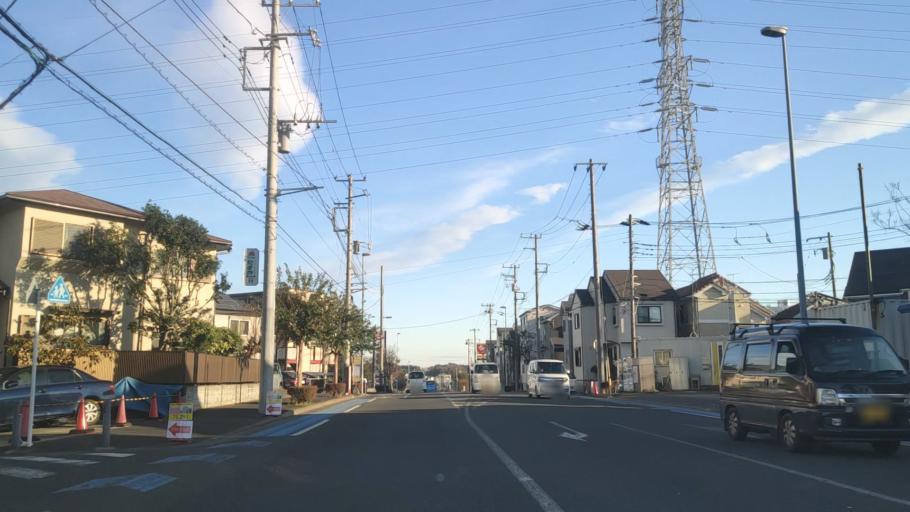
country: JP
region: Kanagawa
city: Fujisawa
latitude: 35.3934
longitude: 139.4902
